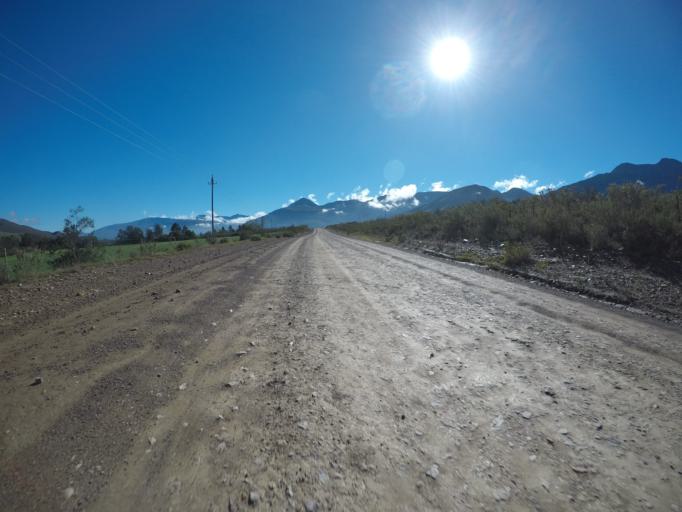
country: ZA
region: Western Cape
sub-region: Overberg District Municipality
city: Caledon
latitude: -34.0825
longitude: 19.6473
